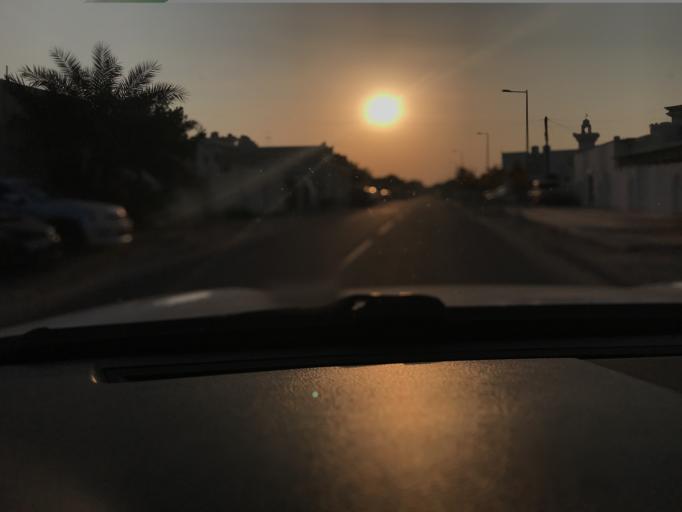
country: QA
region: Baladiyat ad Dawhah
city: Doha
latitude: 25.2515
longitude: 51.5059
